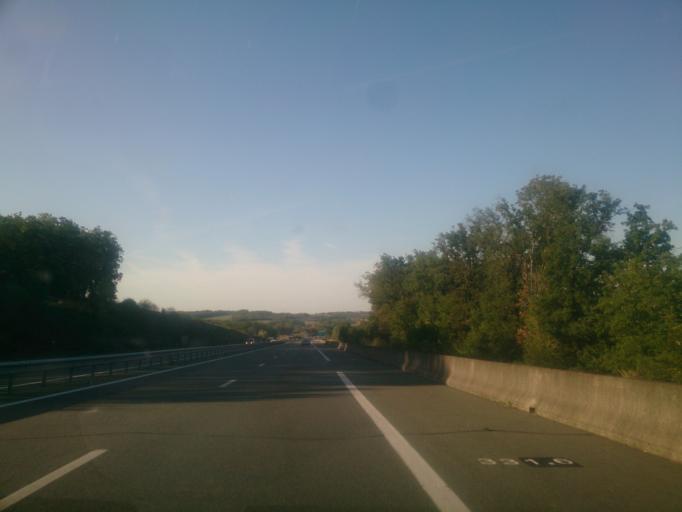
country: FR
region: Midi-Pyrenees
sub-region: Departement du Lot
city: Le Vigan
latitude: 44.6812
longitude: 1.5716
